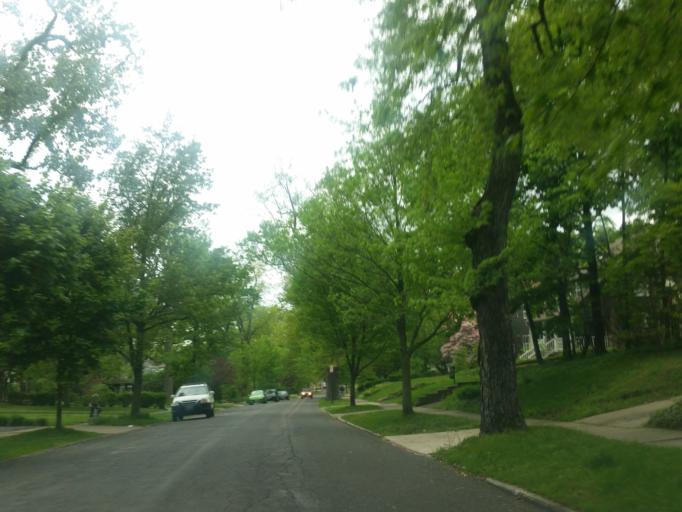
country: US
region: Ohio
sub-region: Cuyahoga County
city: East Cleveland
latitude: 41.4958
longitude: -81.5958
